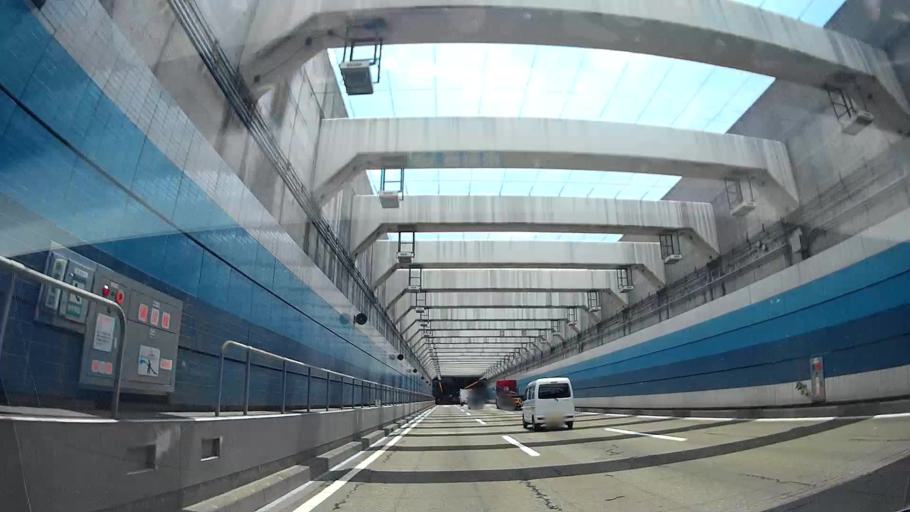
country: JP
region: Kanagawa
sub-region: Kawasaki-shi
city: Kawasaki
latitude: 35.5638
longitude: 139.7702
